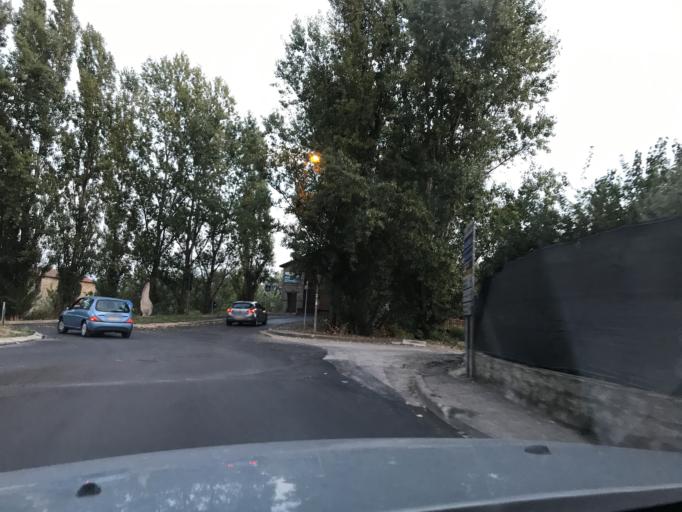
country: IT
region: Umbria
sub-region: Provincia di Perugia
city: Via Lippia
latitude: 43.0914
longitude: 12.4492
